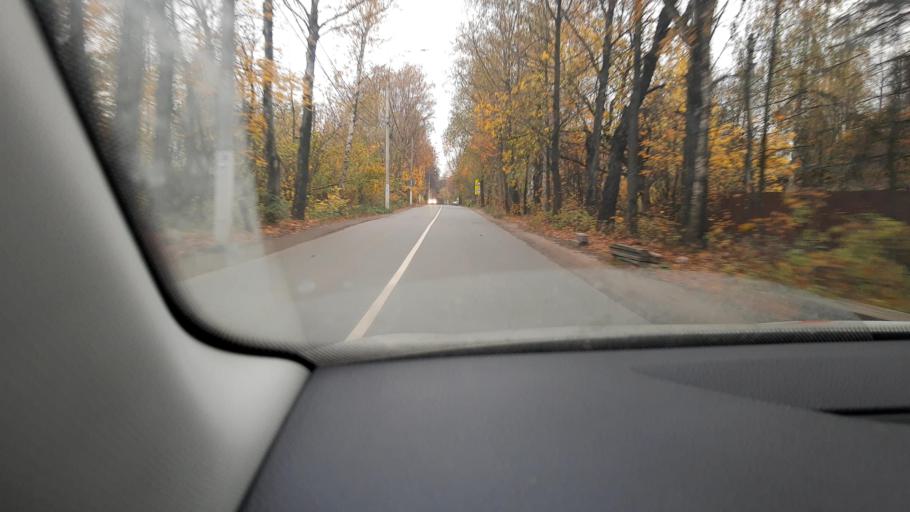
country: RU
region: Moskovskaya
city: Shcherbinka
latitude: 55.5305
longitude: 37.6026
